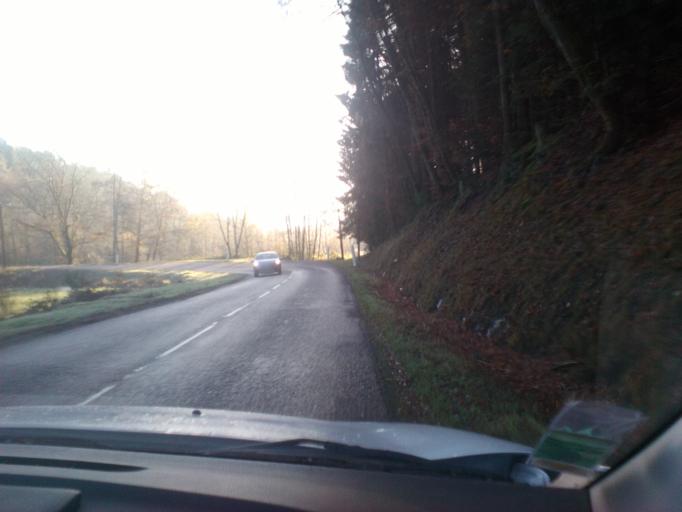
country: FR
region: Lorraine
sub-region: Departement des Vosges
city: Uzemain
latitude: 48.0697
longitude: 6.3128
